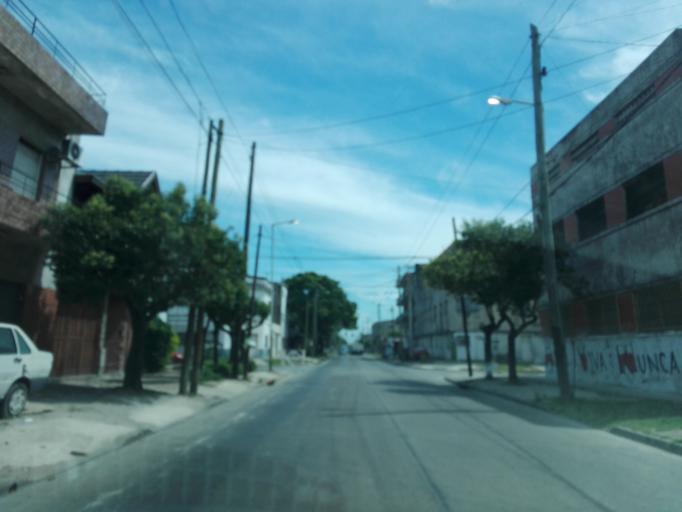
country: AR
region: Buenos Aires
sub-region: Partido de Avellaneda
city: Avellaneda
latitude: -34.6868
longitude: -58.3493
